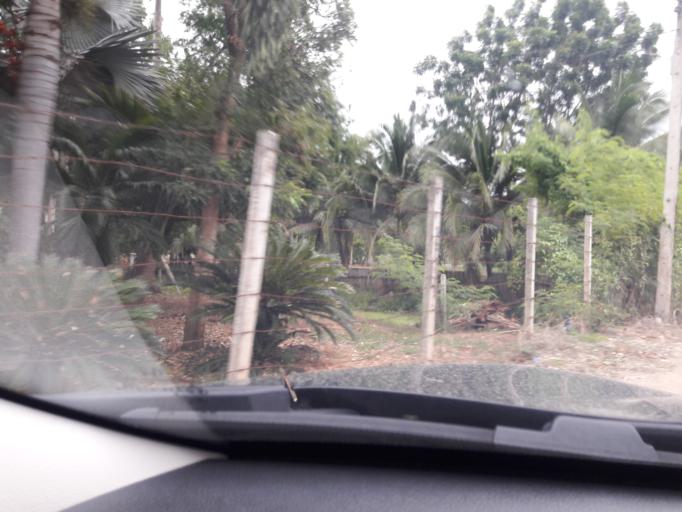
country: TH
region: Ratchaburi
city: Bang Phae
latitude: 13.6099
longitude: 99.9091
